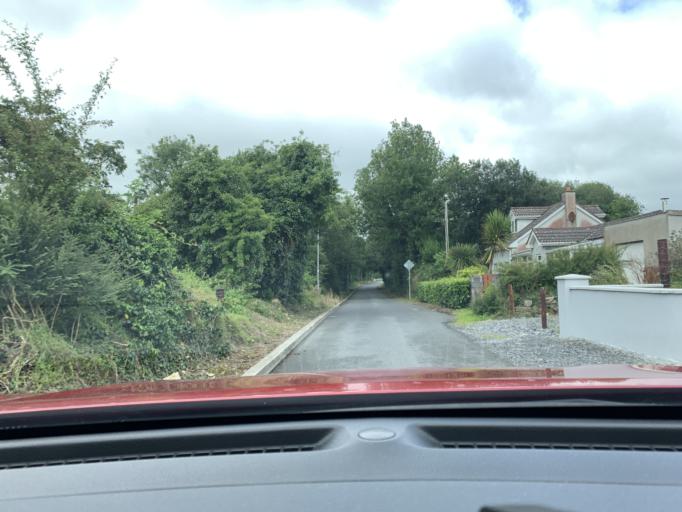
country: IE
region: Connaught
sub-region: Roscommon
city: Boyle
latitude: 53.9845
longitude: -8.2816
